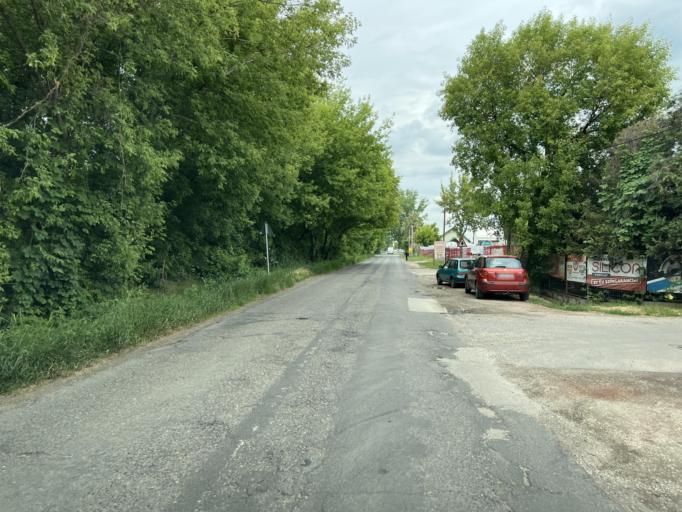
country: HU
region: Pest
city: Nagytarcsa
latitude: 47.5371
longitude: 19.2781
